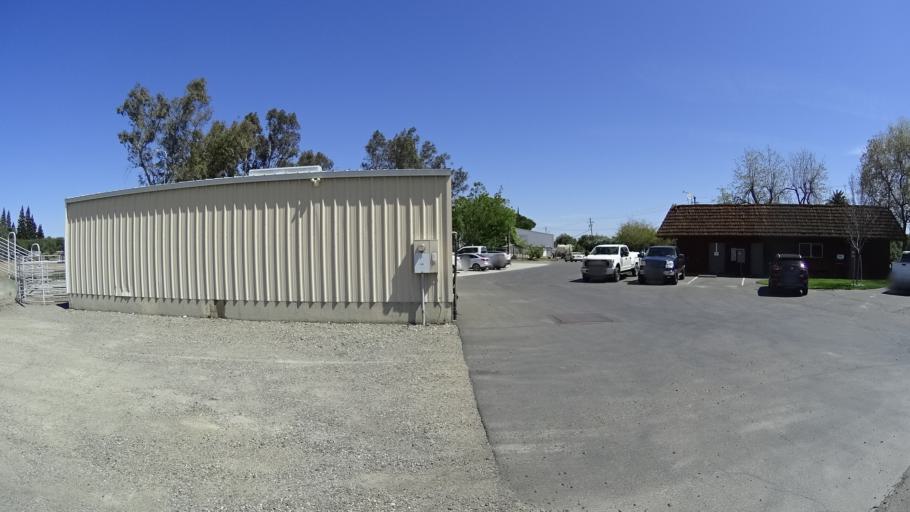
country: US
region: California
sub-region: Glenn County
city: Orland
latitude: 39.7476
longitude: -122.1598
